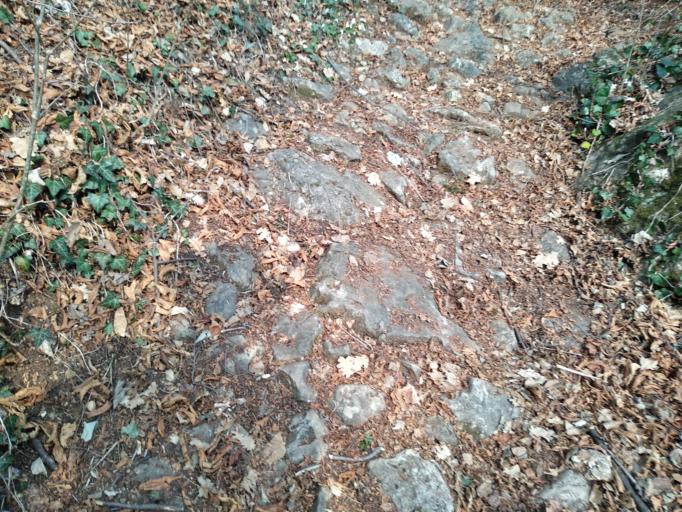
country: IT
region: Veneto
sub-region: Provincia di Vicenza
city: Santorso
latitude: 45.7458
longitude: 11.4024
